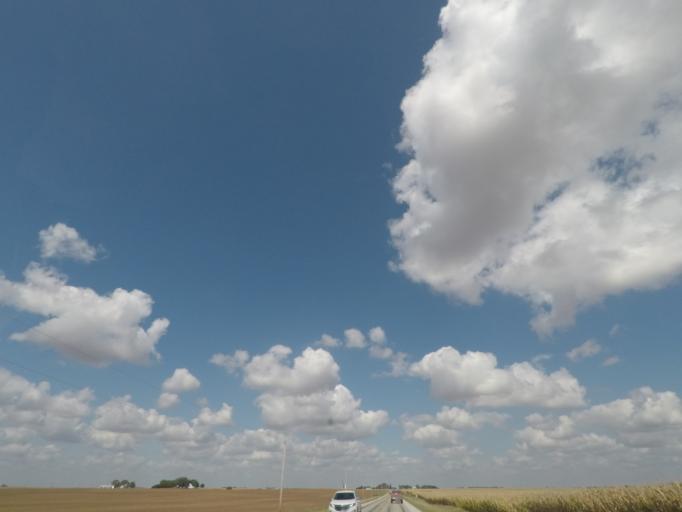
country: US
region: Iowa
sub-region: Story County
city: Nevada
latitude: 42.0273
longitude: -93.4057
